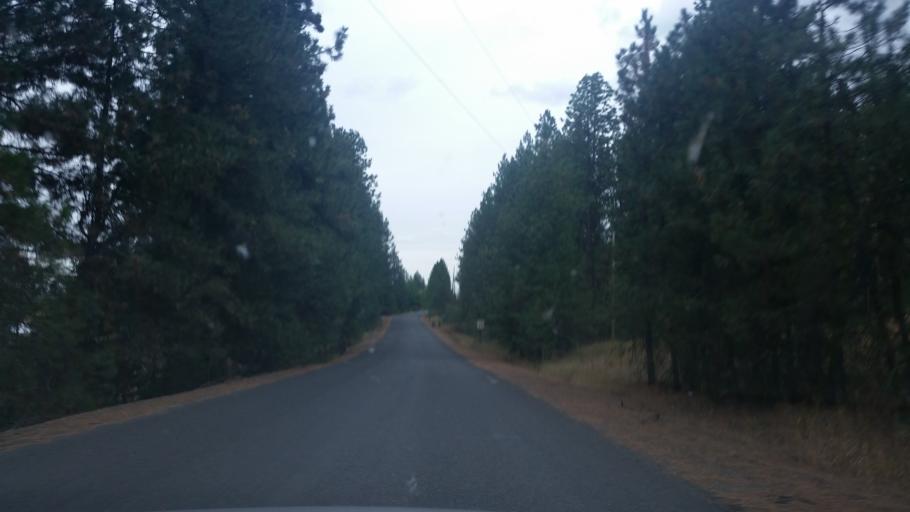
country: US
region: Washington
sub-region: Spokane County
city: Cheney
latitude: 47.5287
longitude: -117.5801
